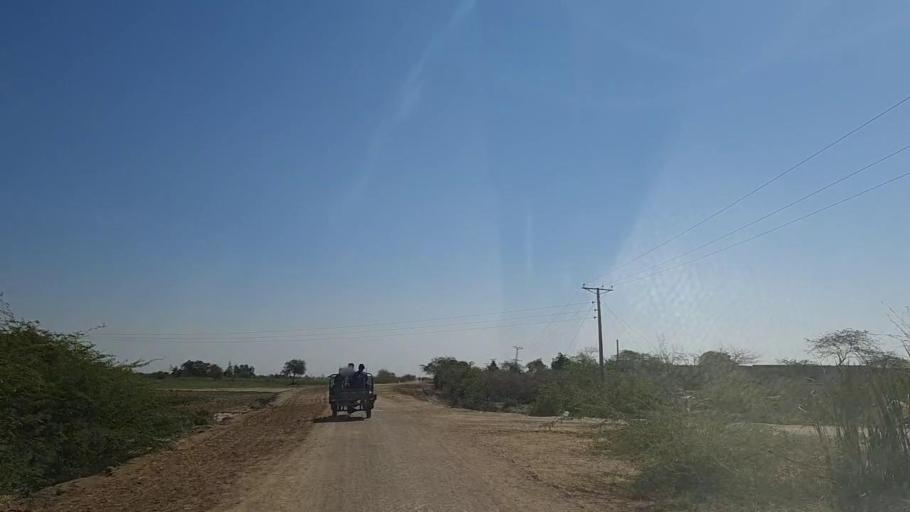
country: PK
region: Sindh
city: Samaro
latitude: 25.3101
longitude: 69.4762
